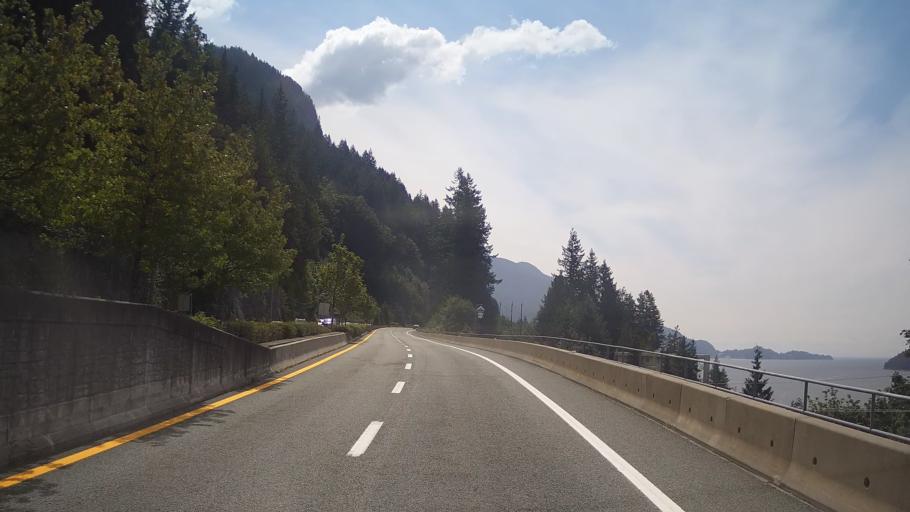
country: CA
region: British Columbia
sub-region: Greater Vancouver Regional District
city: Lions Bay
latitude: 49.4505
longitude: -123.2373
